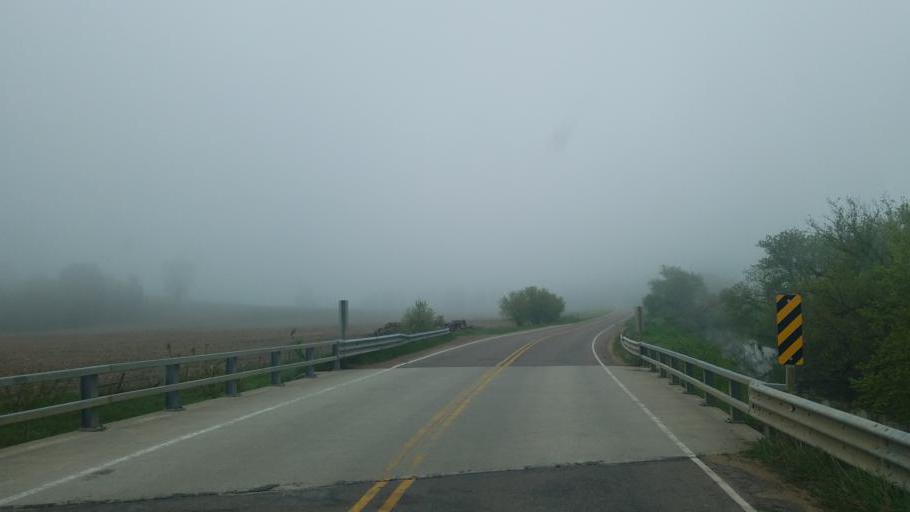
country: US
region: Wisconsin
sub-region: Vernon County
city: Hillsboro
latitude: 43.6385
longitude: -90.3525
